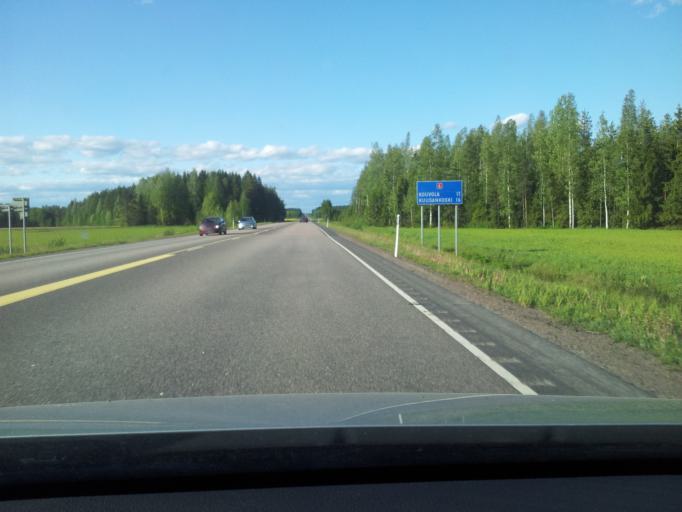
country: FI
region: Kymenlaakso
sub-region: Kouvola
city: Elimaeki
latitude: 60.7944
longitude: 26.5048
